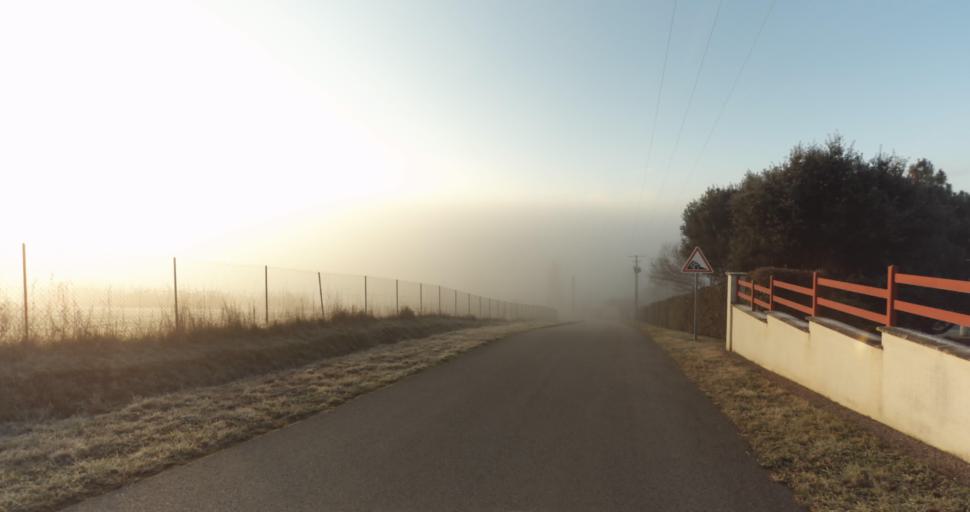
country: FR
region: Limousin
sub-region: Departement de la Haute-Vienne
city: Aixe-sur-Vienne
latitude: 45.7923
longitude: 1.1609
